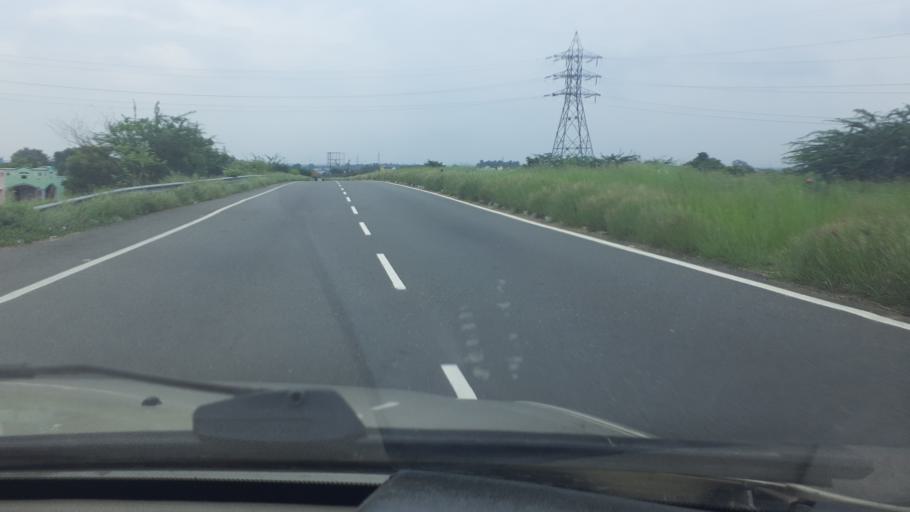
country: IN
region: Tamil Nadu
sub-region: Madurai
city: Tirupparangunram
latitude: 9.8353
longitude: 77.9804
